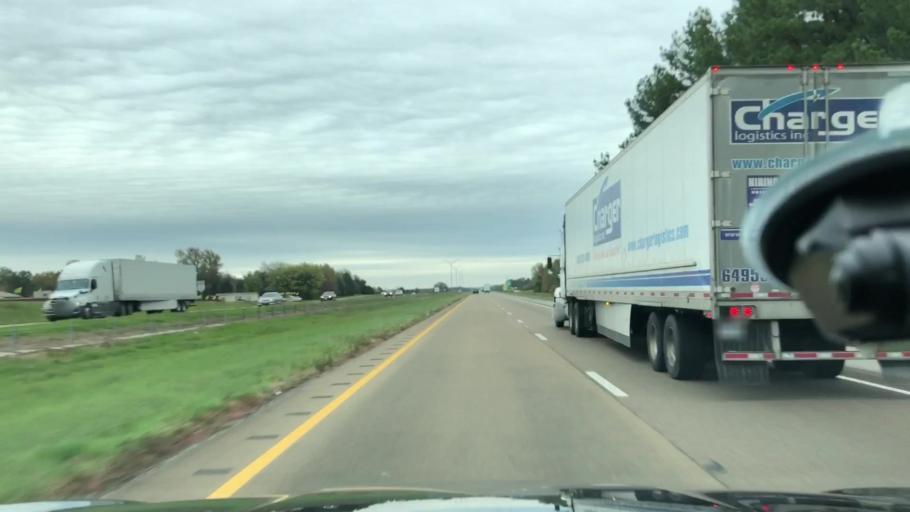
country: US
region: Texas
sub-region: Titus County
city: Mount Pleasant
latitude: 33.2392
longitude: -94.8689
